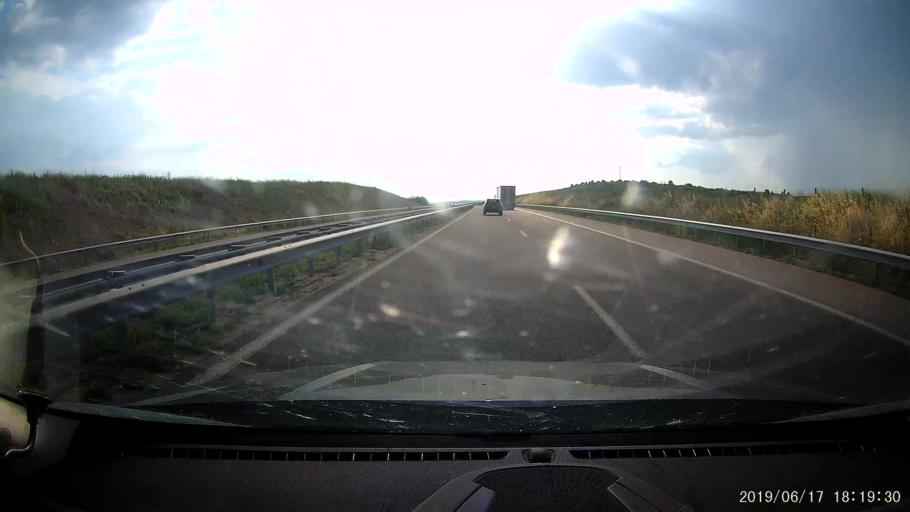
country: BG
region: Khaskovo
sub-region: Obshtina Kharmanli
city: Kharmanli
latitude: 41.9626
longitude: 25.8445
